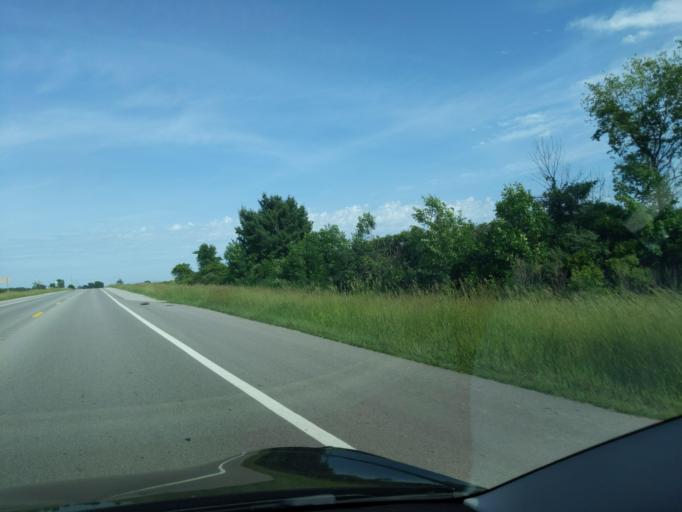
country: US
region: Michigan
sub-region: Muskegon County
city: Twin Lake
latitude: 43.4242
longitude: -86.0586
